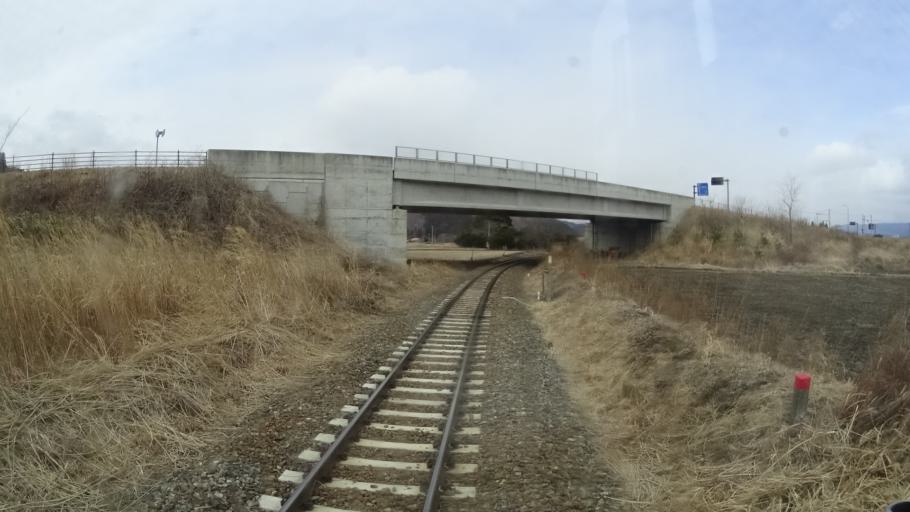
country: JP
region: Iwate
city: Tono
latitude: 39.2905
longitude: 141.5787
